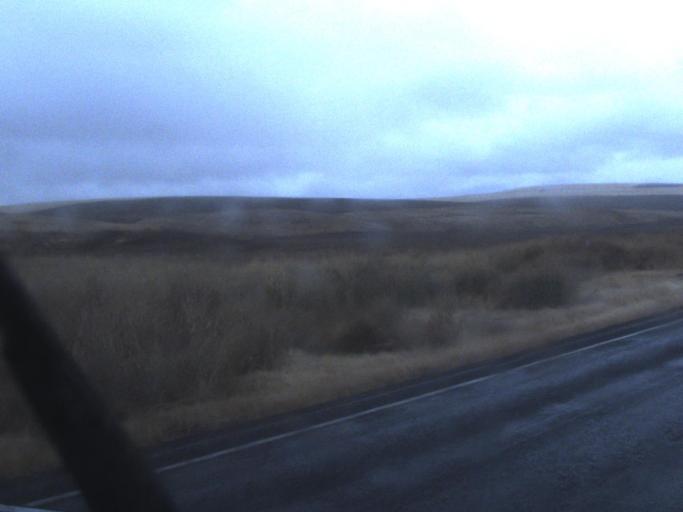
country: US
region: Washington
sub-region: Whitman County
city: Colfax
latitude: 47.1008
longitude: -117.6105
